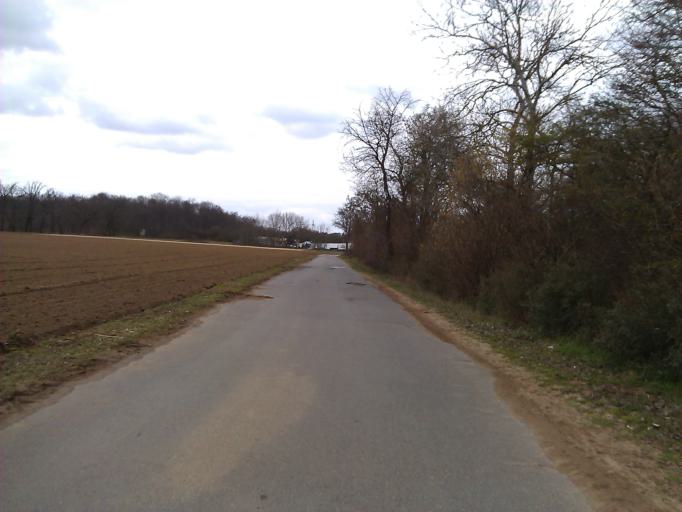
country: DE
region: Hesse
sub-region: Regierungsbezirk Darmstadt
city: Buttelborn
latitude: 49.8896
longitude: 8.5486
